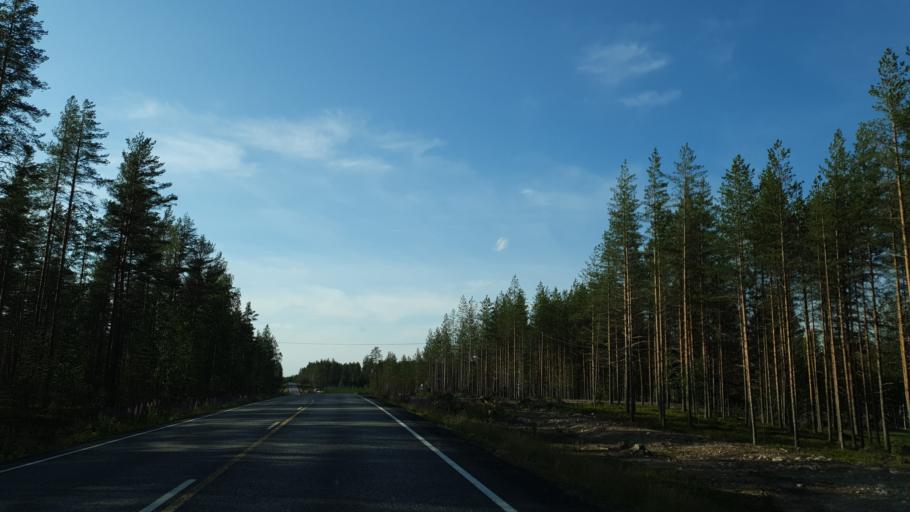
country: FI
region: Kainuu
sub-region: Kehys-Kainuu
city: Kuhmo
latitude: 64.0907
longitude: 29.4809
